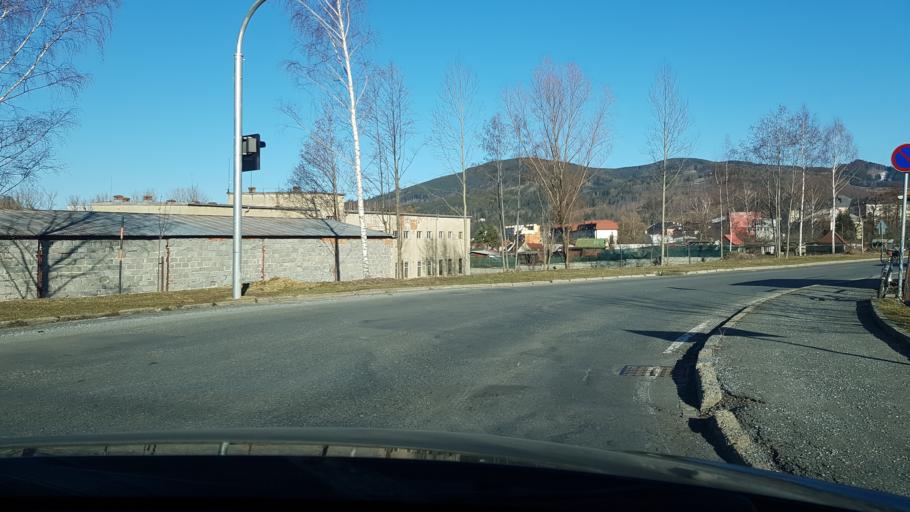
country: CZ
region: Olomoucky
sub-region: Okres Jesenik
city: Jesenik
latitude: 50.2217
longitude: 17.1892
